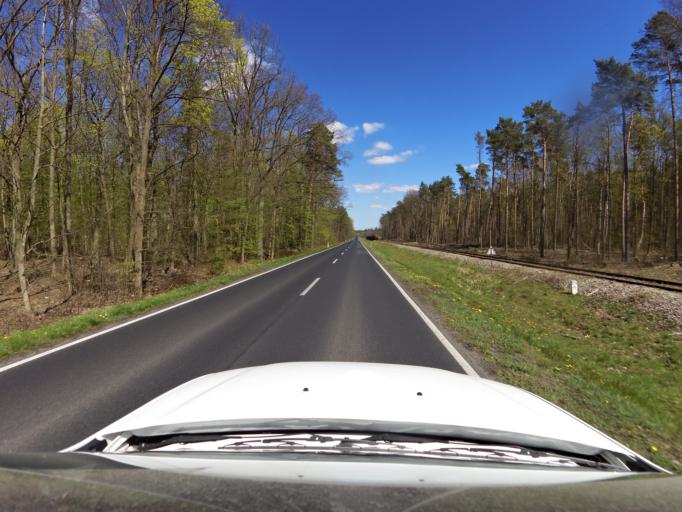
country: PL
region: West Pomeranian Voivodeship
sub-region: Powiat mysliborski
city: Debno
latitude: 52.7541
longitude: 14.7297
